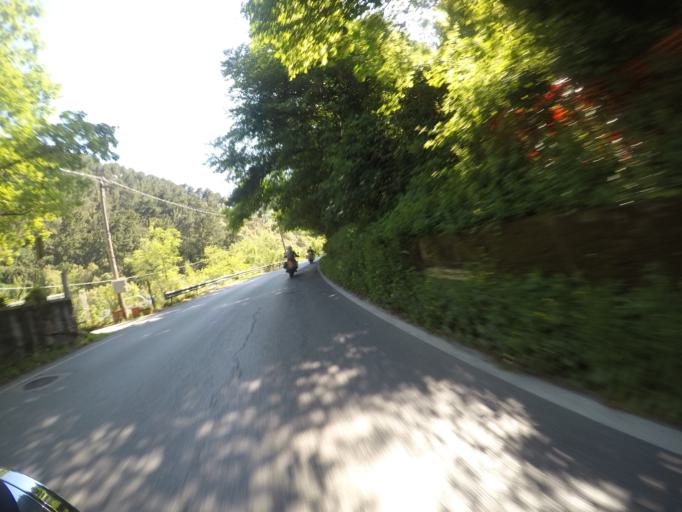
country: IT
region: Tuscany
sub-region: Provincia di Massa-Carrara
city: Montignoso
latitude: 44.0479
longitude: 10.1558
